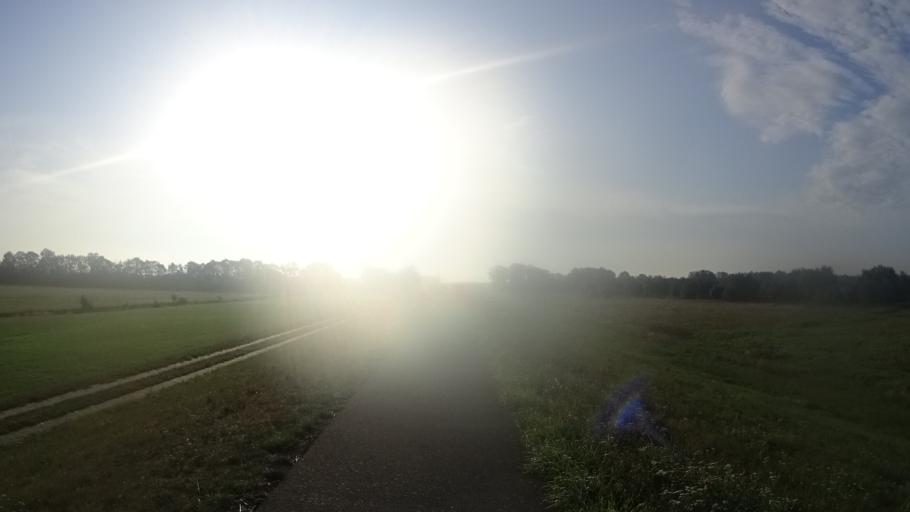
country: DE
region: Brandenburg
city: Lenzen
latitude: 53.0623
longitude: 11.5110
